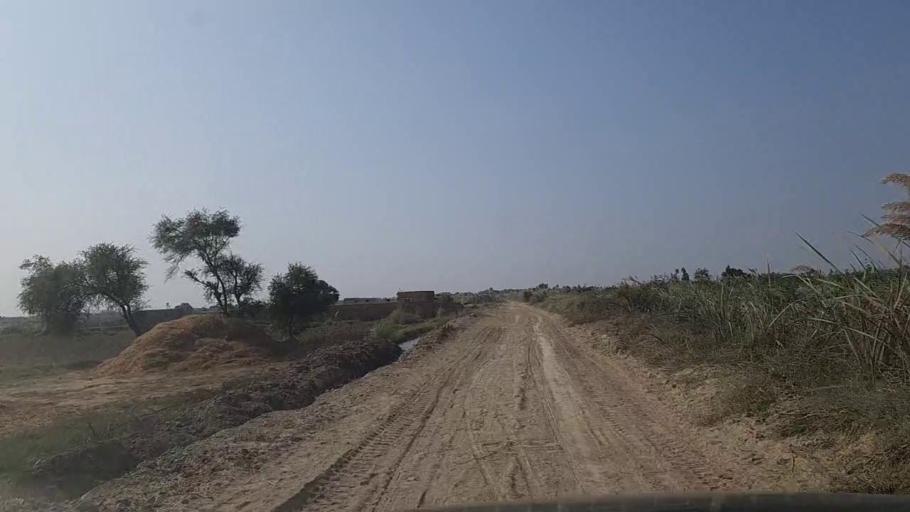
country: PK
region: Sindh
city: Gharo
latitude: 24.7146
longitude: 67.6568
